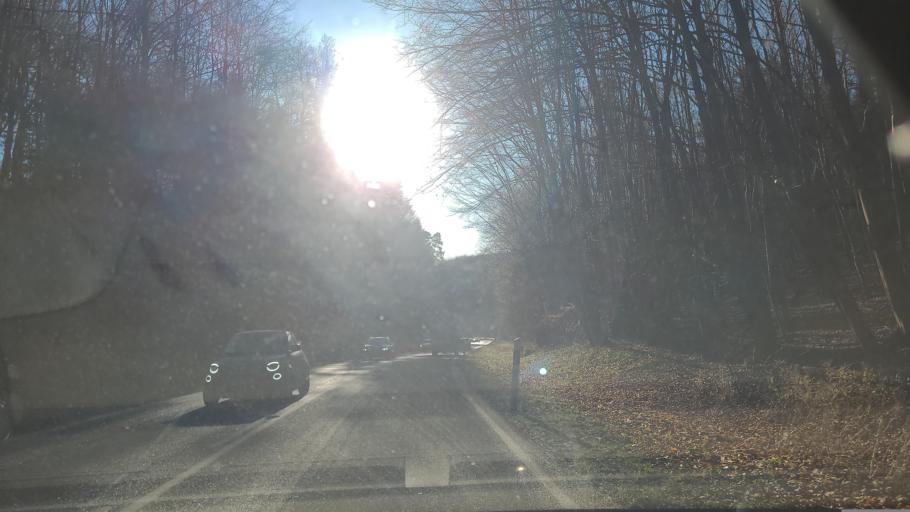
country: LU
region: Luxembourg
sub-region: Canton de Luxembourg
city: Strassen
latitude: 49.6370
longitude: 6.0852
